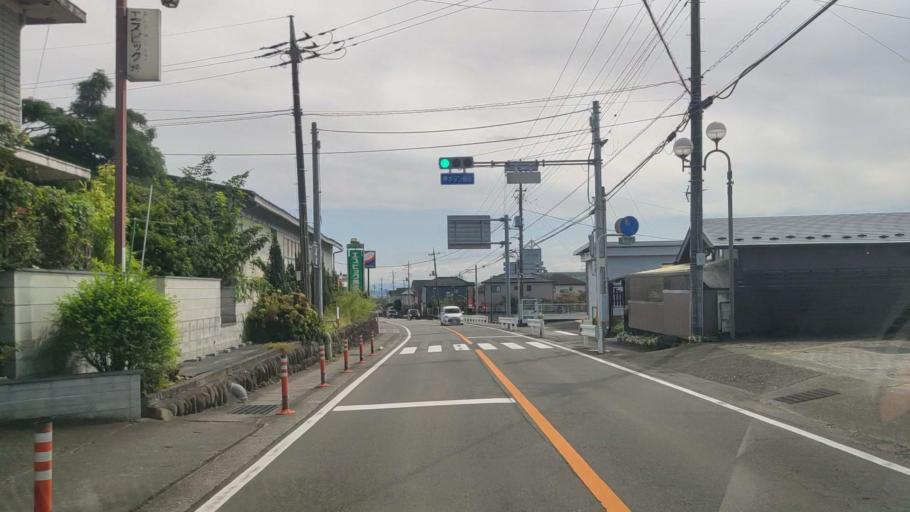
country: JP
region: Gunma
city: Kanekomachi
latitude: 36.3889
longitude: 138.9586
